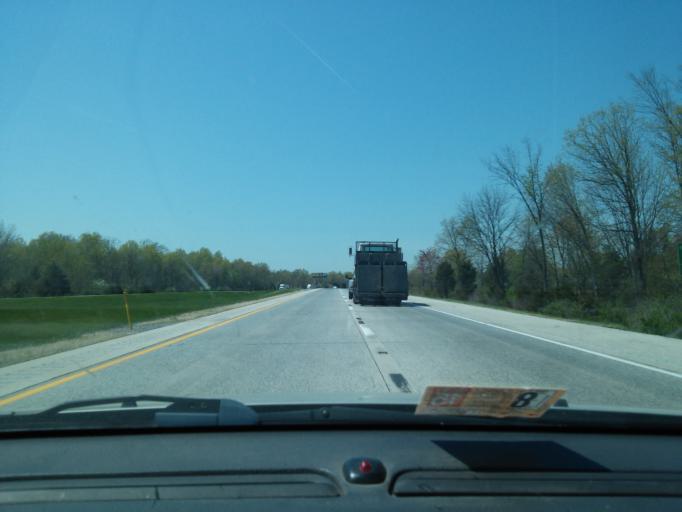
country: US
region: Pennsylvania
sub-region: Lebanon County
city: Jonestown
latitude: 40.4323
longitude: -76.4979
